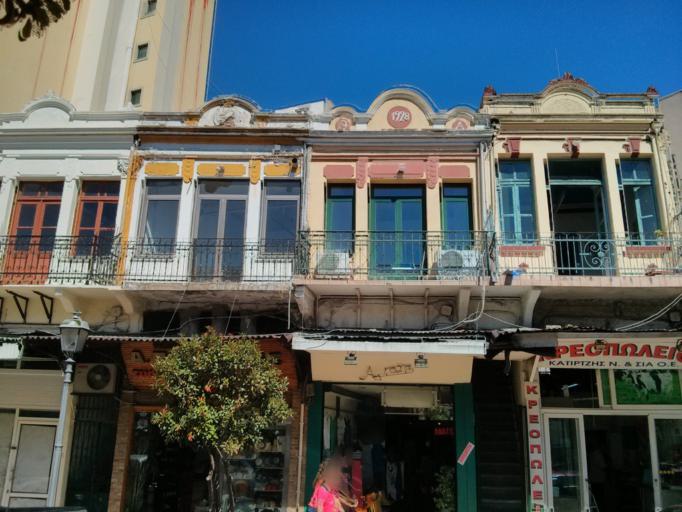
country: GR
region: East Macedonia and Thrace
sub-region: Nomos Kavalas
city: Kavala
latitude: 40.9370
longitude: 24.4141
